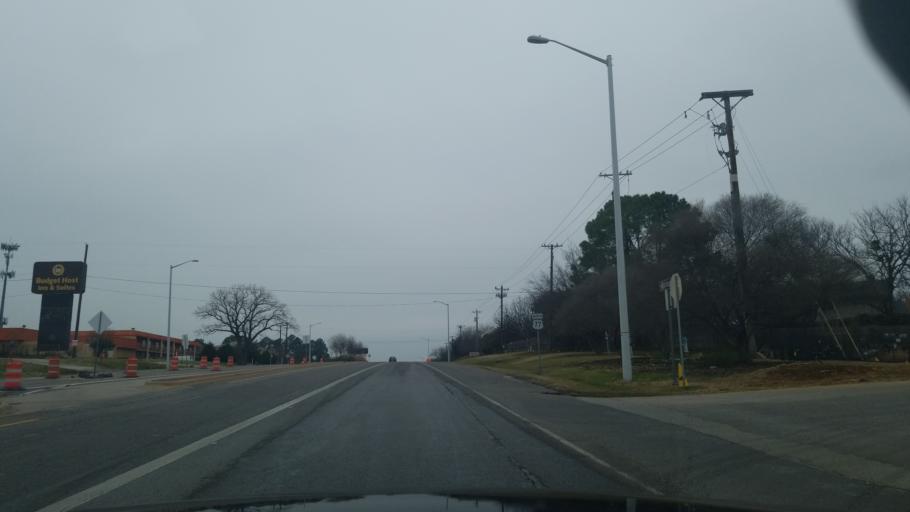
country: US
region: Texas
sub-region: Denton County
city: Denton
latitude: 33.1930
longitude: -97.1161
